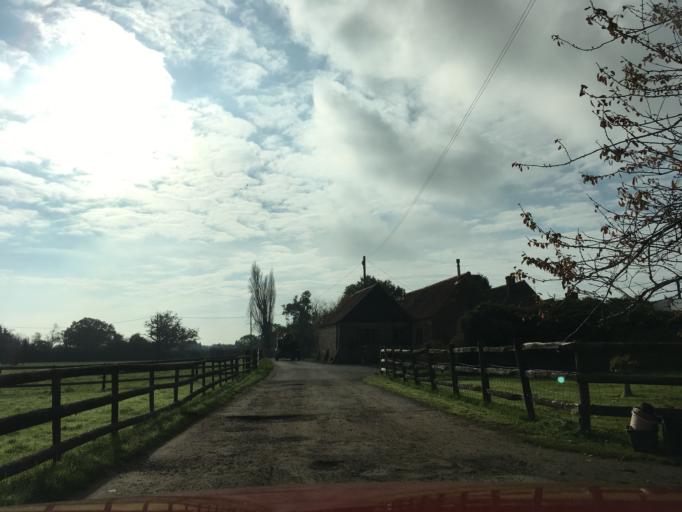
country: GB
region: England
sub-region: South Gloucestershire
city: Wickwar
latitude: 51.5818
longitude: -2.4339
